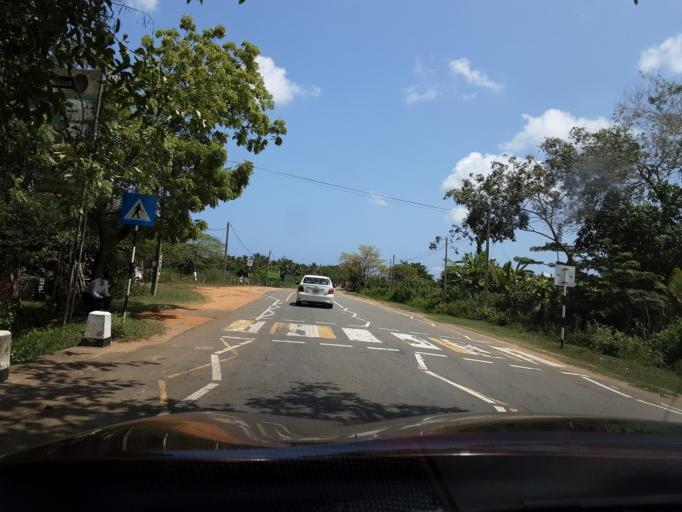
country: LK
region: Southern
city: Tangalla
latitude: 6.2381
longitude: 81.2272
